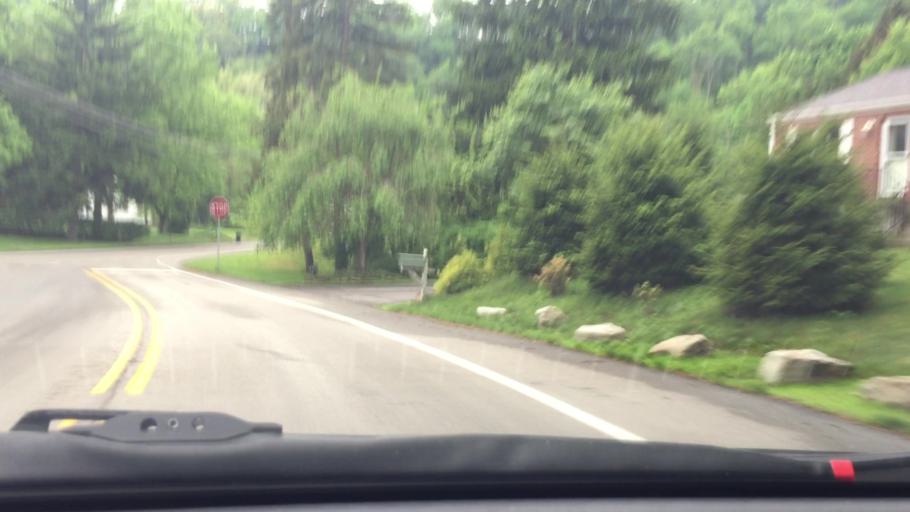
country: US
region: Pennsylvania
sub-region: Allegheny County
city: Glenshaw
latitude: 40.5318
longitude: -79.9602
